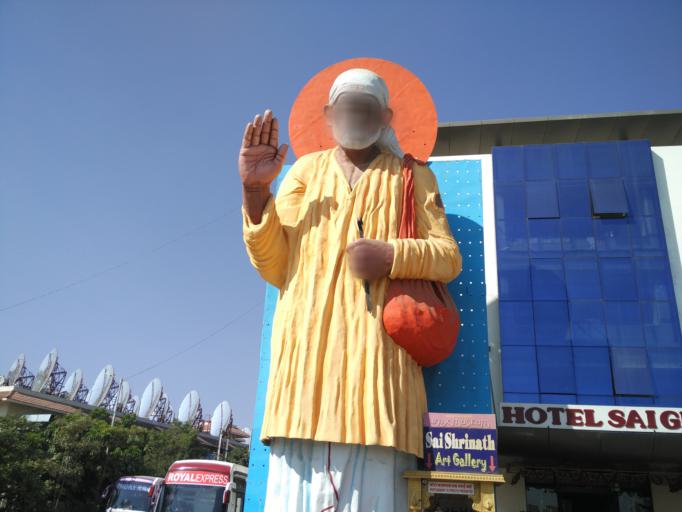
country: IN
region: Maharashtra
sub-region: Ahmadnagar
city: Shirdi
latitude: 19.7700
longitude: 74.4723
